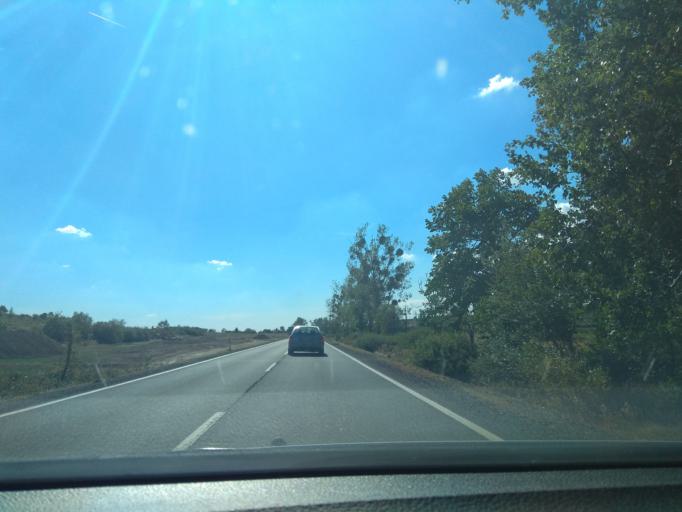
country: HU
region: Borsod-Abauj-Zemplen
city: Sarospatak
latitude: 48.3591
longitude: 21.5915
